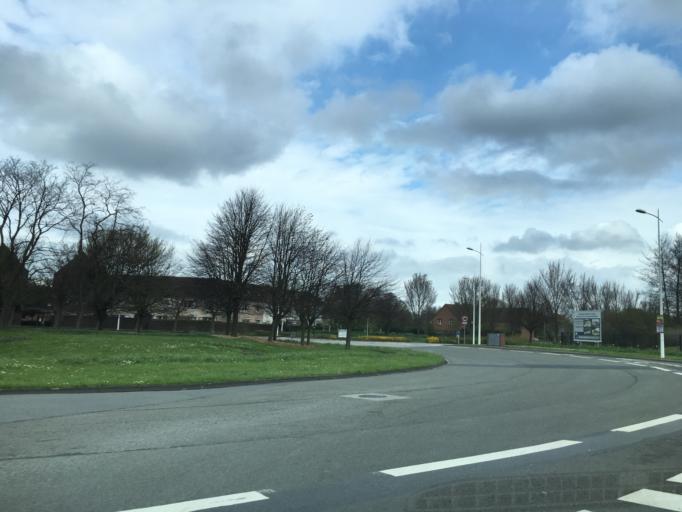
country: FR
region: Nord-Pas-de-Calais
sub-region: Departement du Nord
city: Grande-Synthe
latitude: 51.0075
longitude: 2.3110
